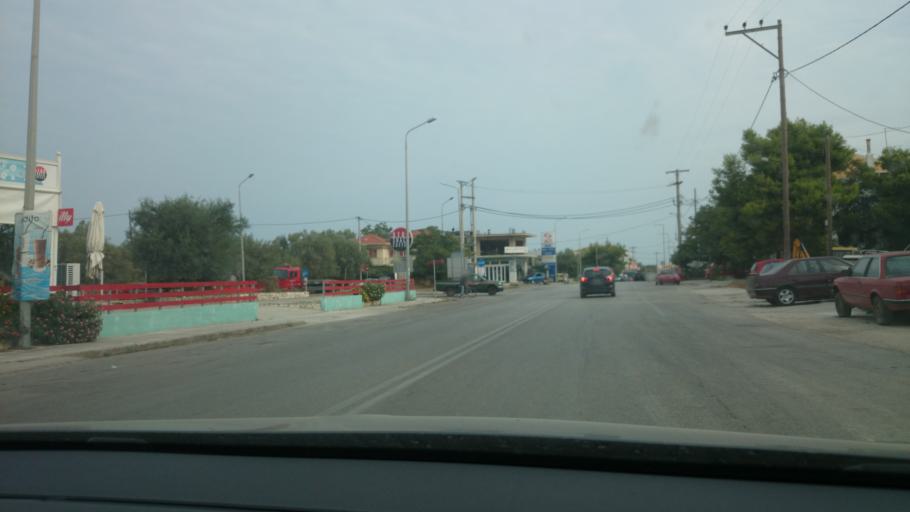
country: GR
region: Ionian Islands
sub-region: Lefkada
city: Lefkada
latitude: 38.8201
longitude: 20.7024
